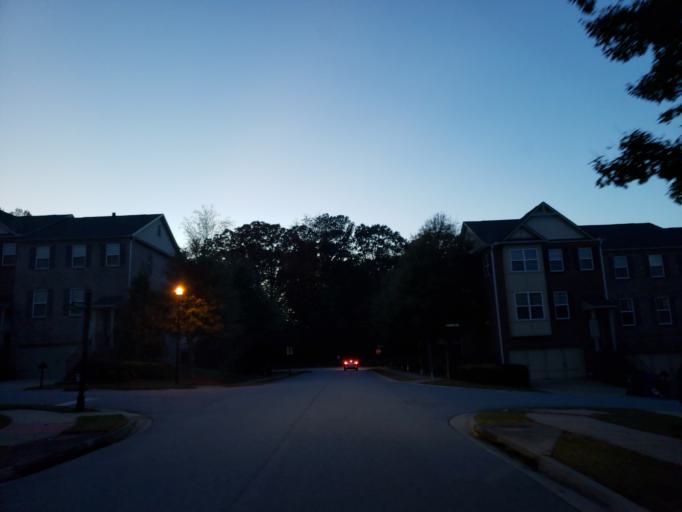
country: US
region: Georgia
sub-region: DeKalb County
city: Chamblee
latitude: 33.8949
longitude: -84.3210
